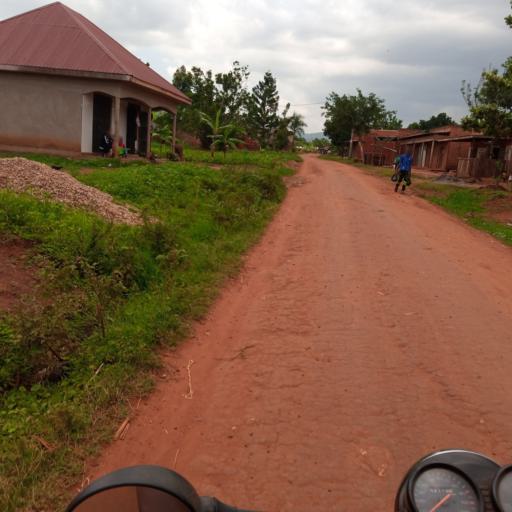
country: UG
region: Eastern Region
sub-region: Mbale District
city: Mbale
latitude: 1.1228
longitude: 34.1821
